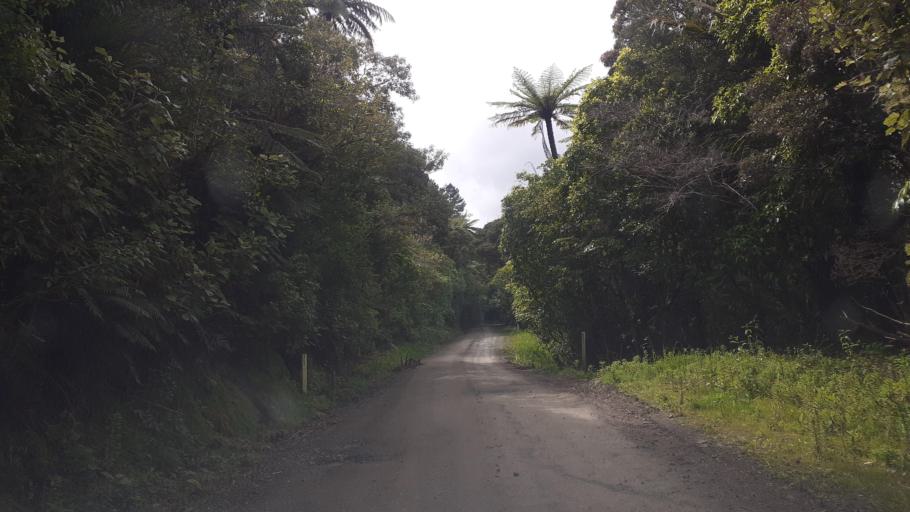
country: NZ
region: Northland
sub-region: Far North District
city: Waimate North
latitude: -35.5728
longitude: 173.5627
